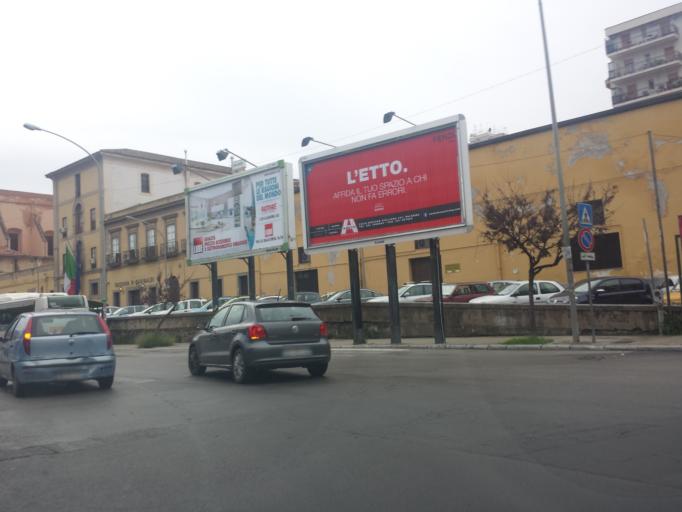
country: IT
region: Sicily
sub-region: Palermo
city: Palermo
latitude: 38.1109
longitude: 13.3499
